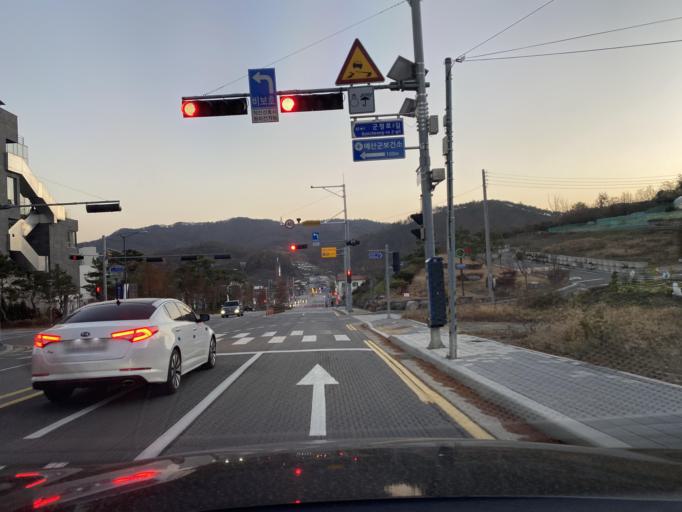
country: KR
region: Chungcheongnam-do
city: Yesan
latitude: 36.6819
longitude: 126.8435
